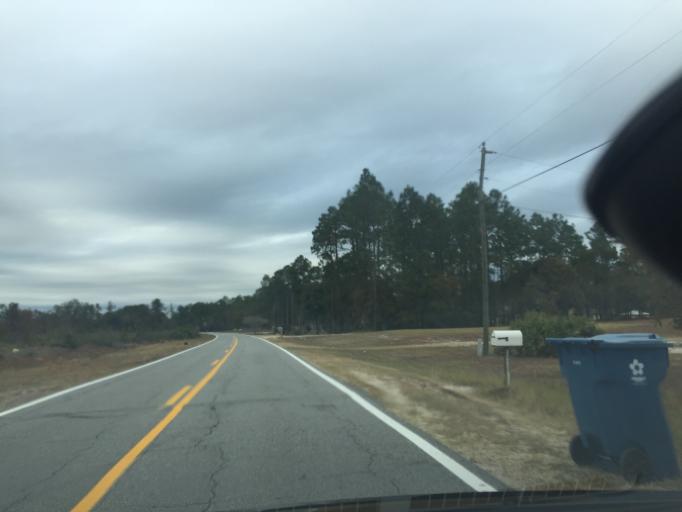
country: US
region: Georgia
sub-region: Chatham County
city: Bloomingdale
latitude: 32.0926
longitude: -81.3760
